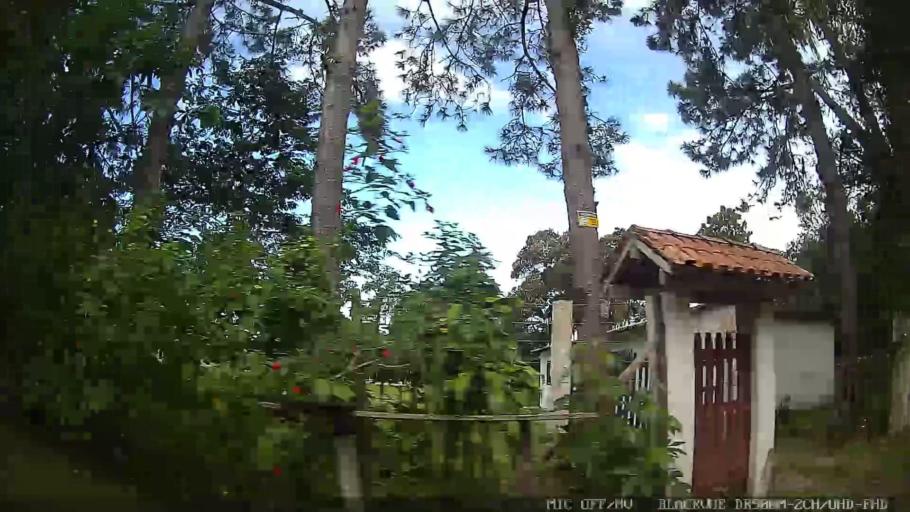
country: BR
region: Sao Paulo
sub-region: Iguape
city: Iguape
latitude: -24.6952
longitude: -47.5337
